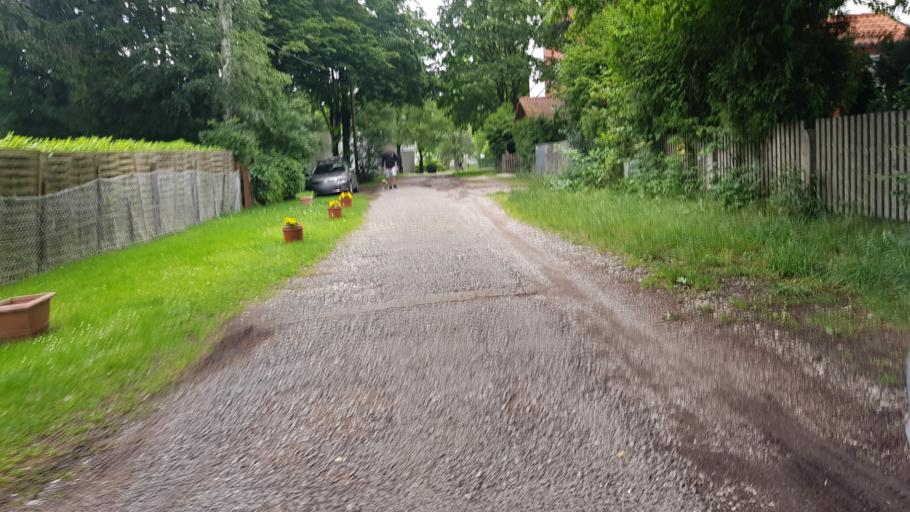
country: DE
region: Bavaria
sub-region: Upper Bavaria
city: Pasing
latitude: 48.1474
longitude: 11.4301
